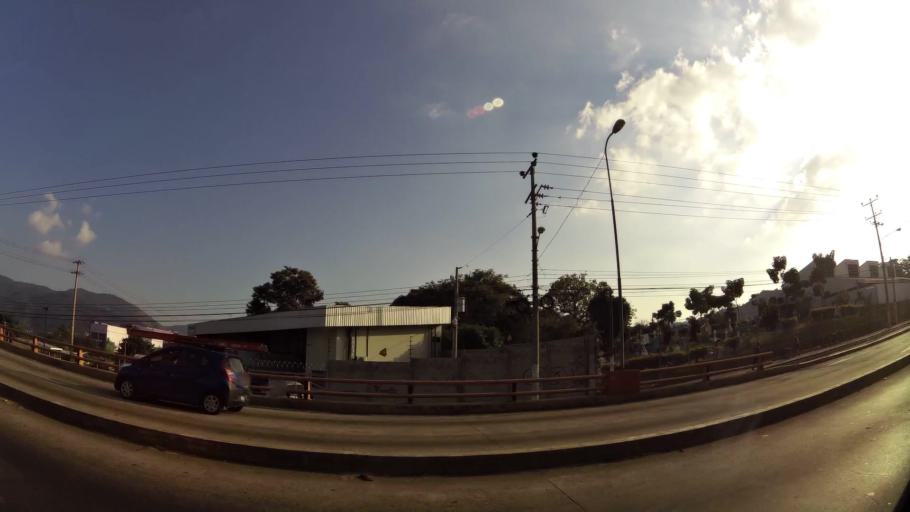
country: SV
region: San Salvador
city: San Salvador
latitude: 13.6924
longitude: -89.2063
